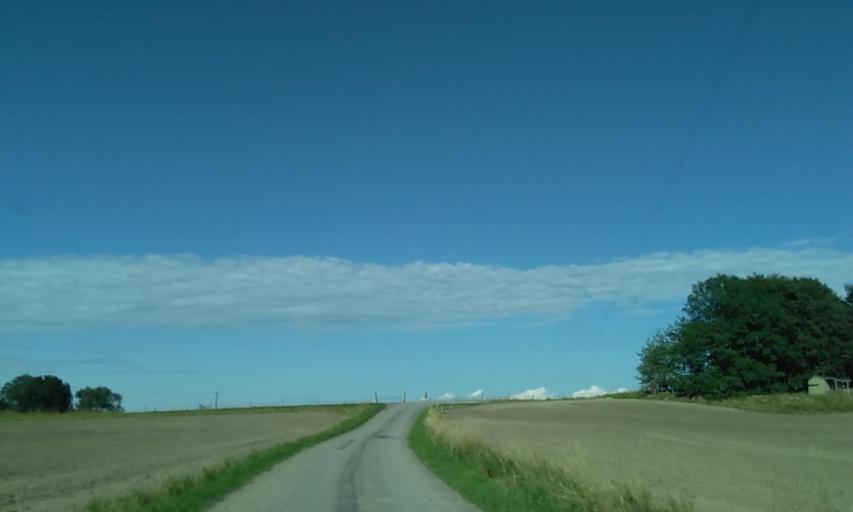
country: SE
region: Vaestra Goetaland
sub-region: Lidkopings Kommun
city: Lidkoping
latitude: 58.5743
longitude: 13.0214
